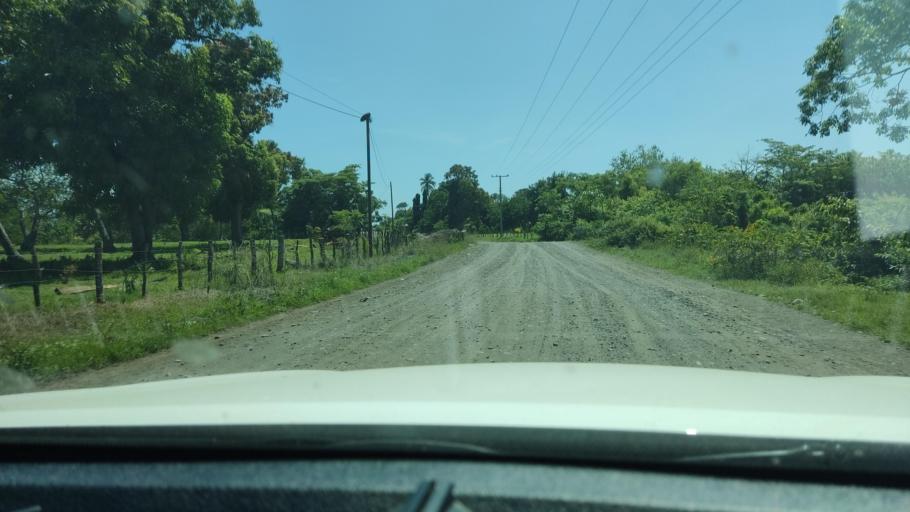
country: SV
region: Ahuachapan
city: San Francisco Menendez
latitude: 13.7655
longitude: -90.1609
